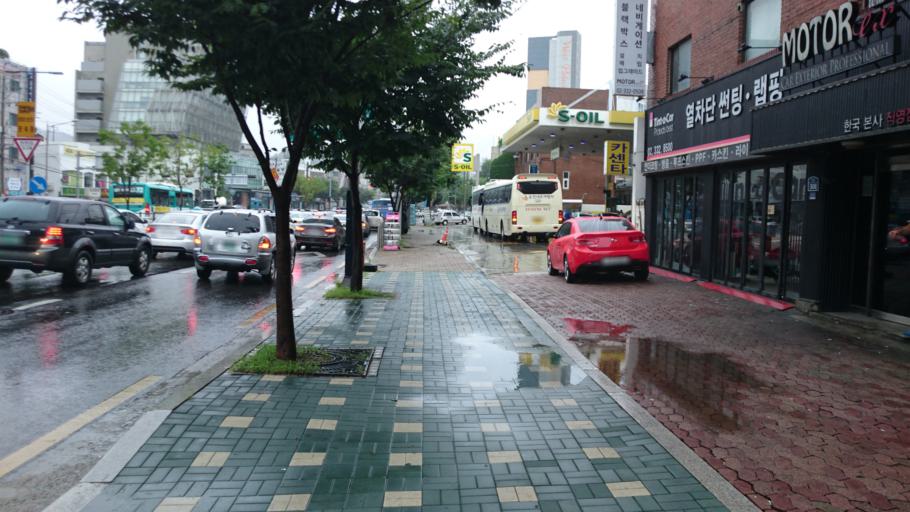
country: KR
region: Seoul
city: Seoul
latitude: 37.5662
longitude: 126.9244
